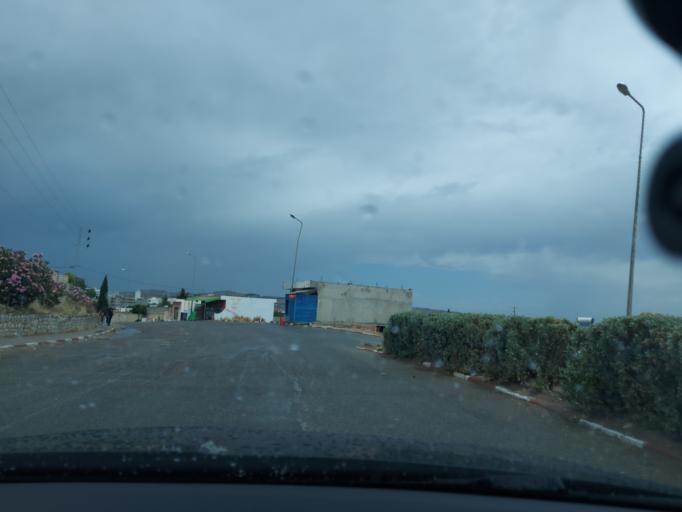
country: TN
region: Silyanah
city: Maktar
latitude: 35.8563
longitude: 9.2101
